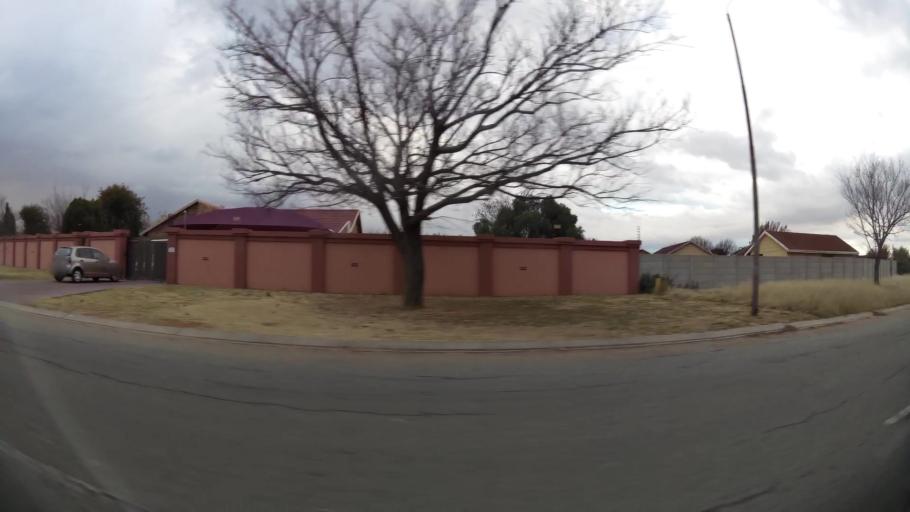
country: ZA
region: Orange Free State
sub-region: Lejweleputswa District Municipality
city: Welkom
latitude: -27.9468
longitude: 26.7236
